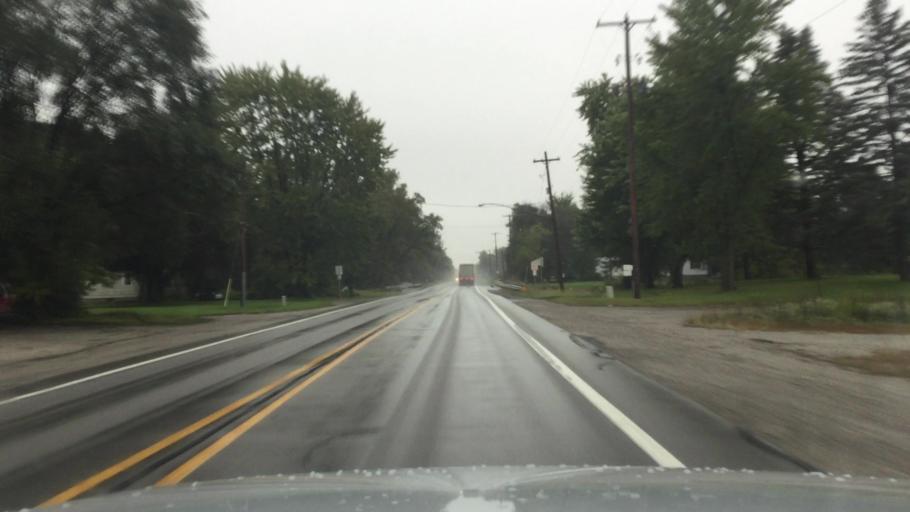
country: US
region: Michigan
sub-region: Saginaw County
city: Saginaw
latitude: 43.3862
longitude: -83.9555
